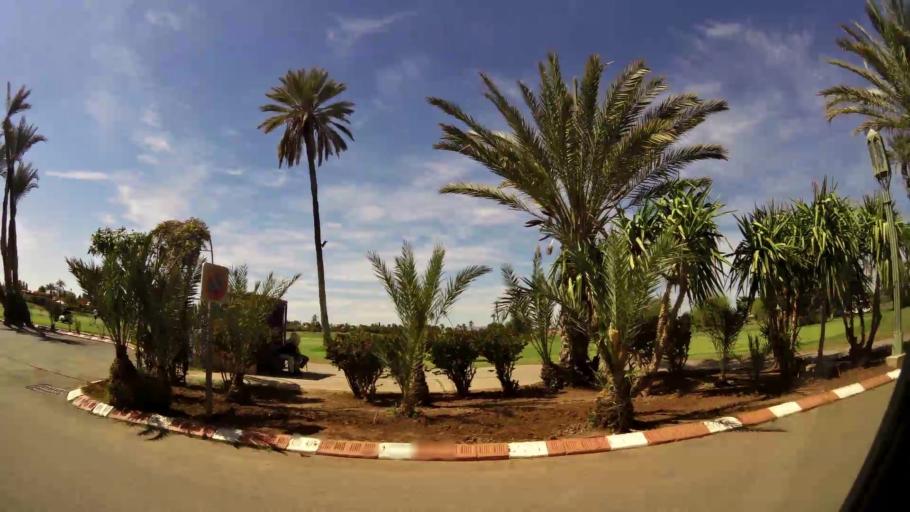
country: MA
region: Marrakech-Tensift-Al Haouz
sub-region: Marrakech
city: Marrakesh
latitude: 31.6125
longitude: -7.9362
